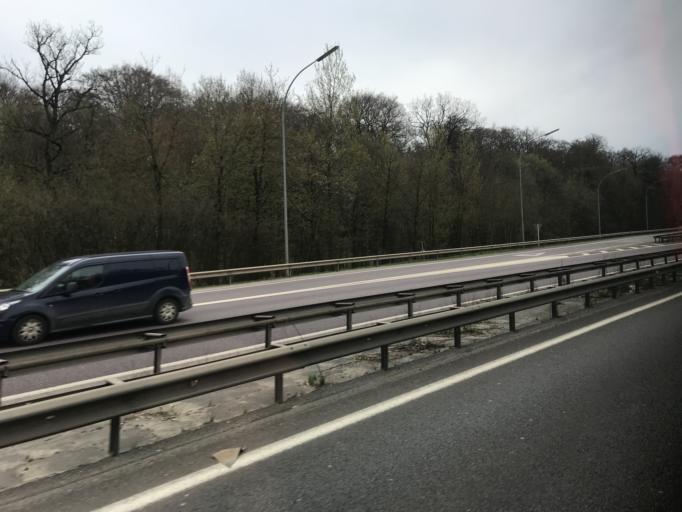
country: LU
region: Luxembourg
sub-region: Canton d'Esch-sur-Alzette
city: Leudelange
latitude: 49.5716
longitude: 6.0880
